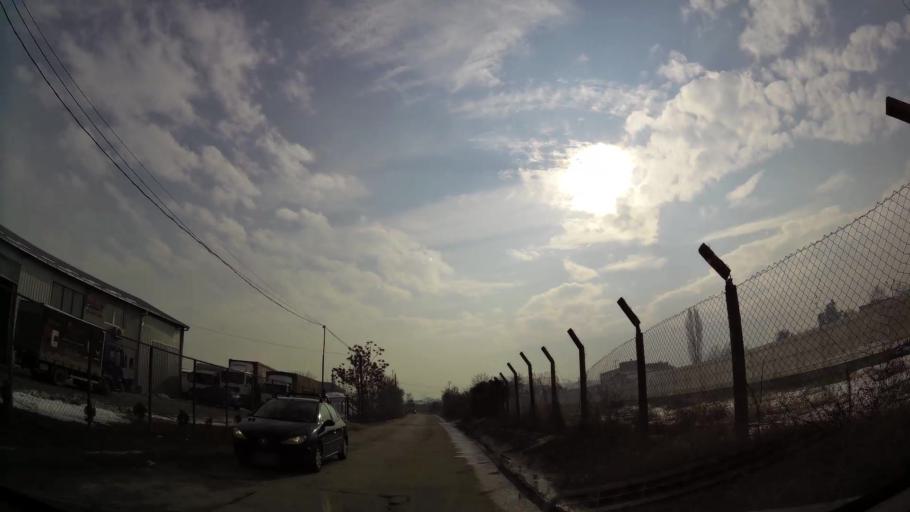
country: MK
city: Krushopek
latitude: 42.0160
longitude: 21.3687
